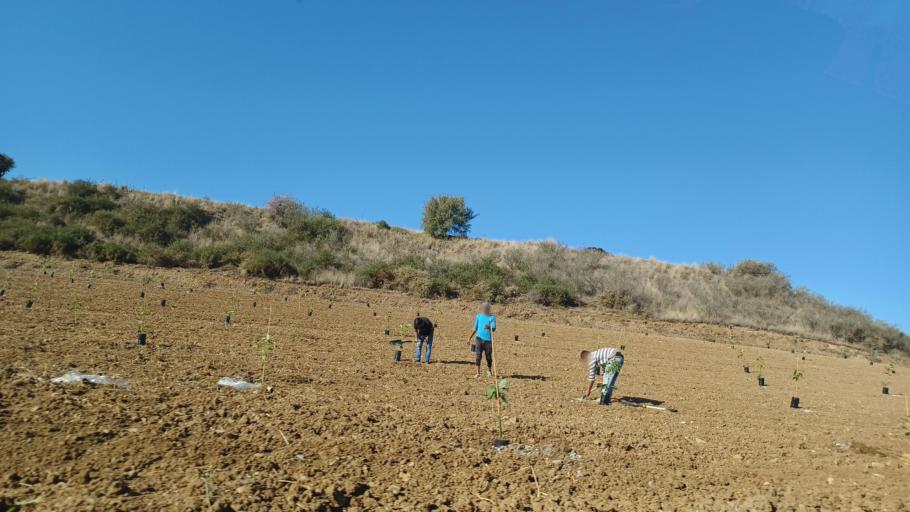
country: CY
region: Pafos
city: Polis
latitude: 35.0165
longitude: 32.4242
